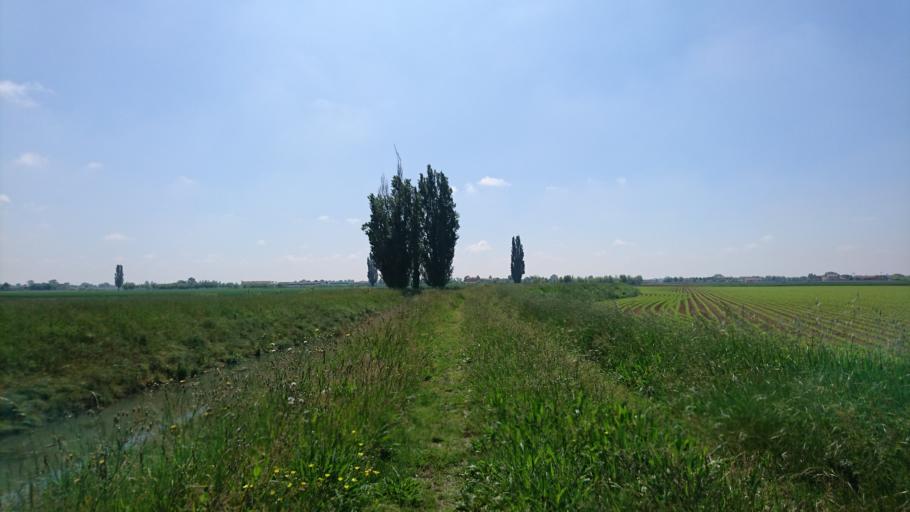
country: IT
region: Veneto
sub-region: Provincia di Padova
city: Casalserugo
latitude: 45.3369
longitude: 11.9242
